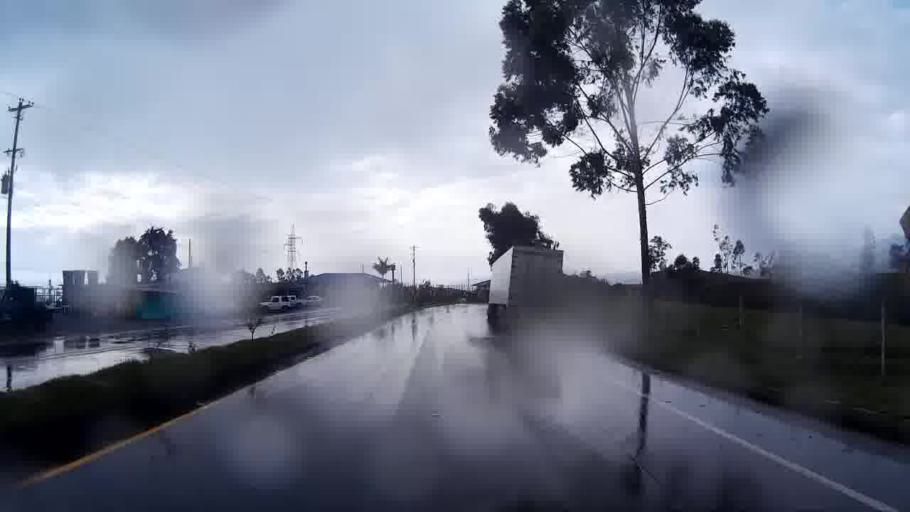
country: CO
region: Quindio
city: Salento
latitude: 4.6783
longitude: -75.6033
